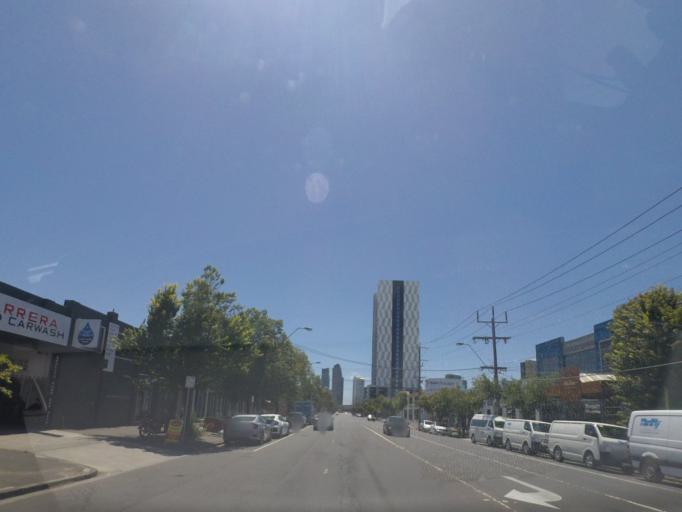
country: AU
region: Victoria
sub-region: Port Phillip
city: Port Melbourne
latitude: -37.8324
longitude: 144.9518
